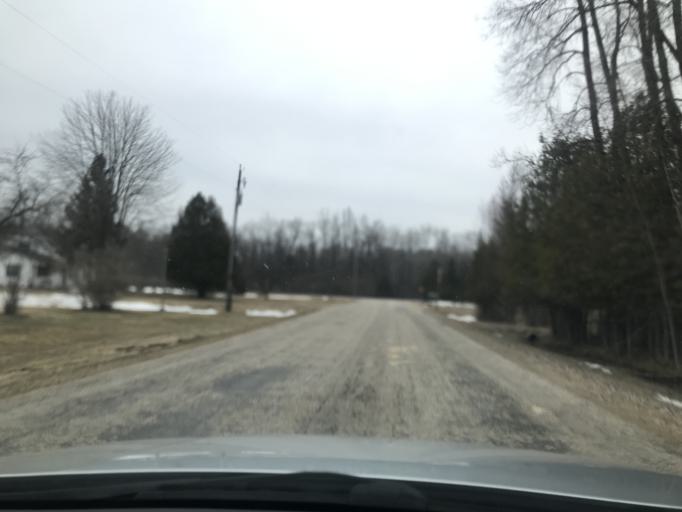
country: US
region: Wisconsin
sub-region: Marinette County
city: Peshtigo
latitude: 45.0866
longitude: -87.9325
